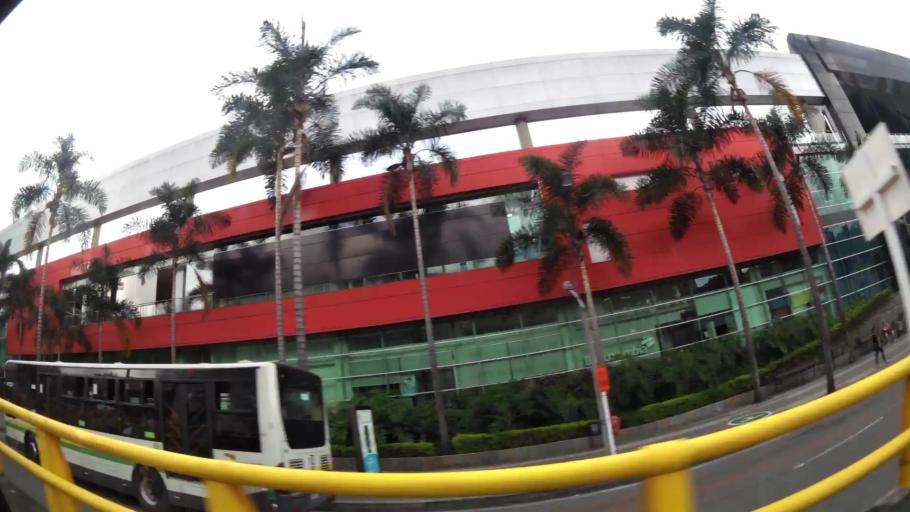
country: CO
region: Antioquia
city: Medellin
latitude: 6.2291
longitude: -75.5697
